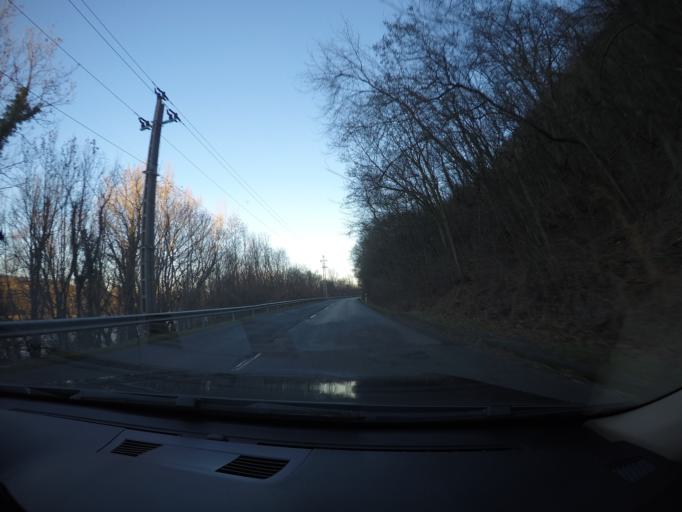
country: HU
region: Pest
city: Visegrad
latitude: 47.8035
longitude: 18.9872
